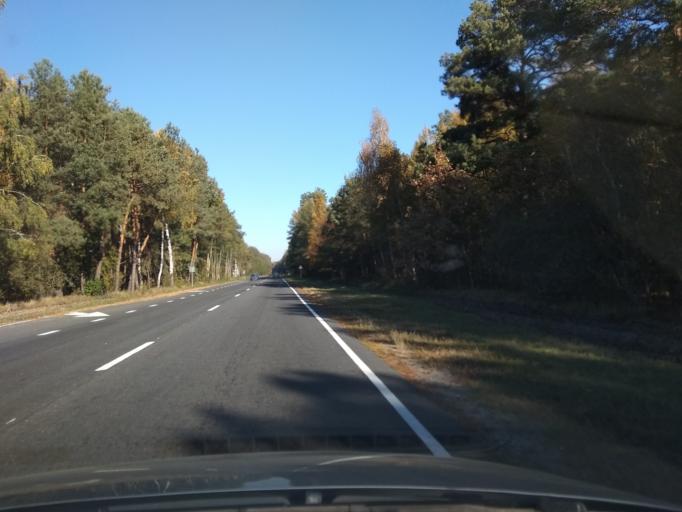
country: BY
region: Brest
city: Kobryn
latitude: 52.0575
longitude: 24.2809
